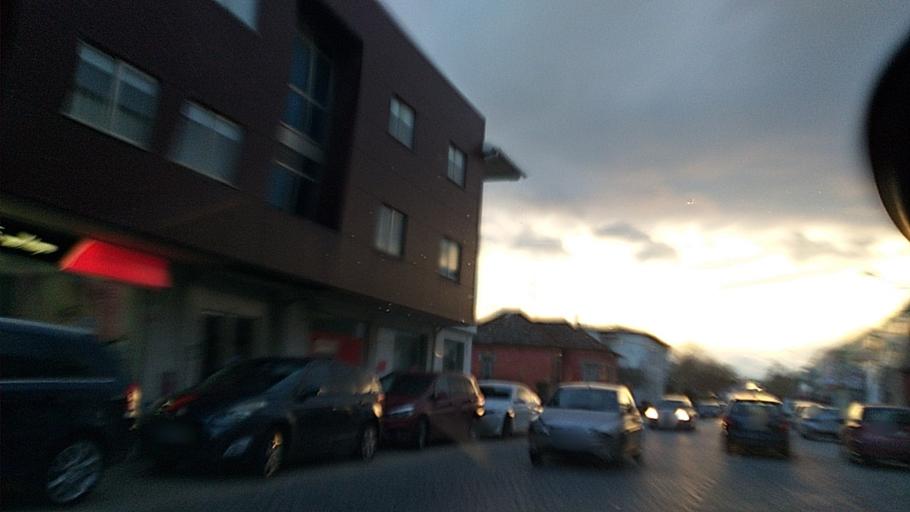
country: PT
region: Guarda
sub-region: Guarda
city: Sequeira
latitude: 40.5557
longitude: -7.2422
